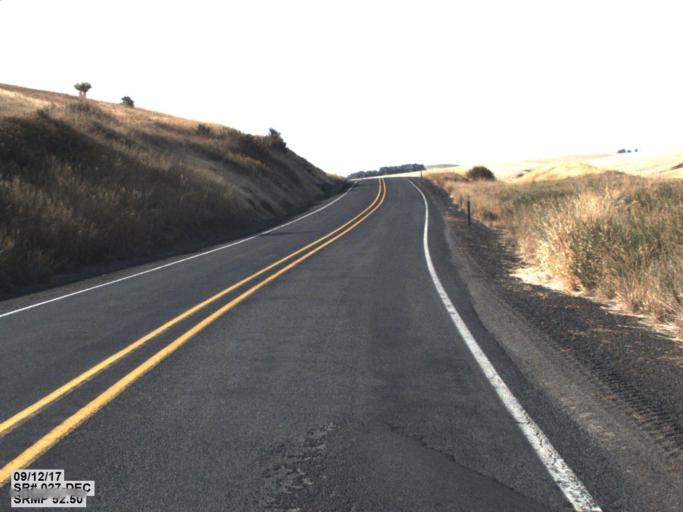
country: US
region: Idaho
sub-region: Benewah County
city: Plummer
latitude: 47.2527
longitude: -117.1303
